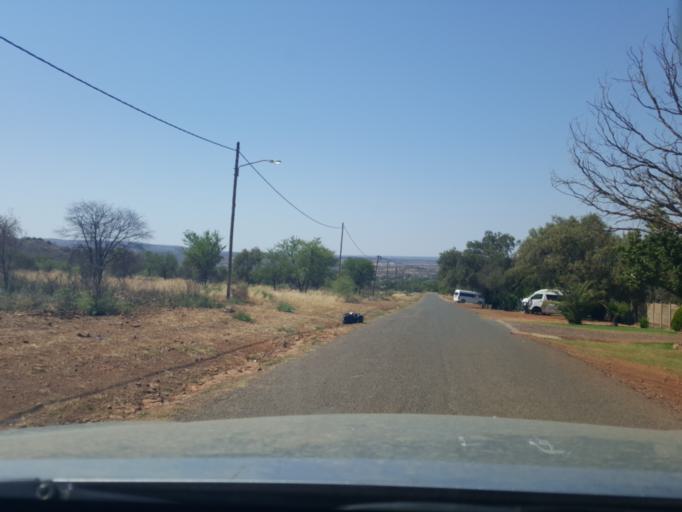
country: ZA
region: North-West
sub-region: Ngaka Modiri Molema District Municipality
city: Zeerust
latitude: -25.5323
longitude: 26.0816
